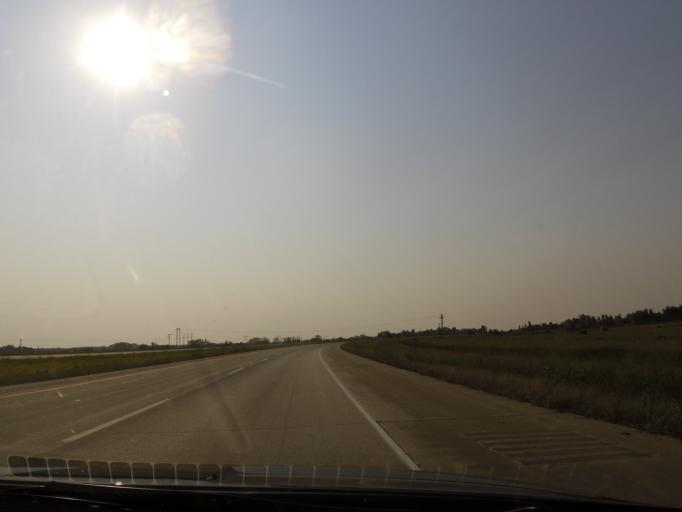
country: US
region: North Dakota
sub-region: Grand Forks County
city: Grand Forks
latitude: 48.0950
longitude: -97.1731
